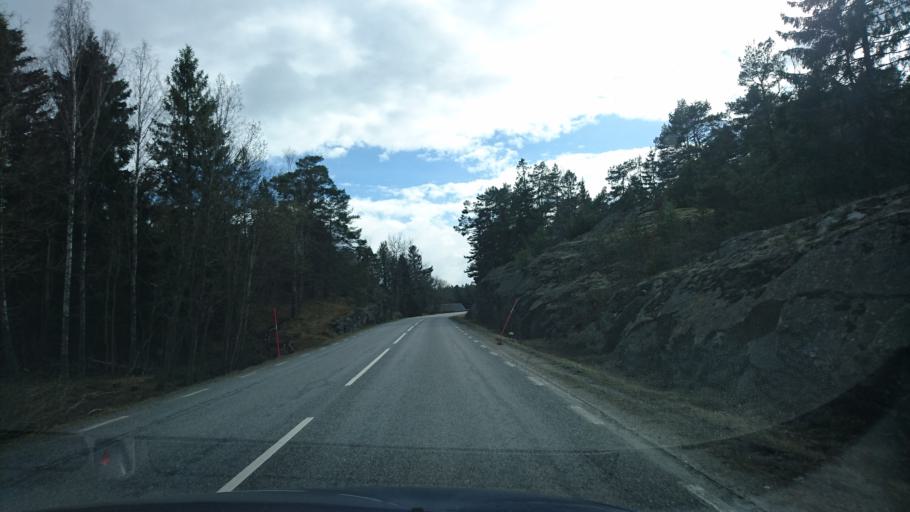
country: SE
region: Stockholm
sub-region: Nynashamns Kommun
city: Nynashamn
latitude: 58.9530
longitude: 18.0141
